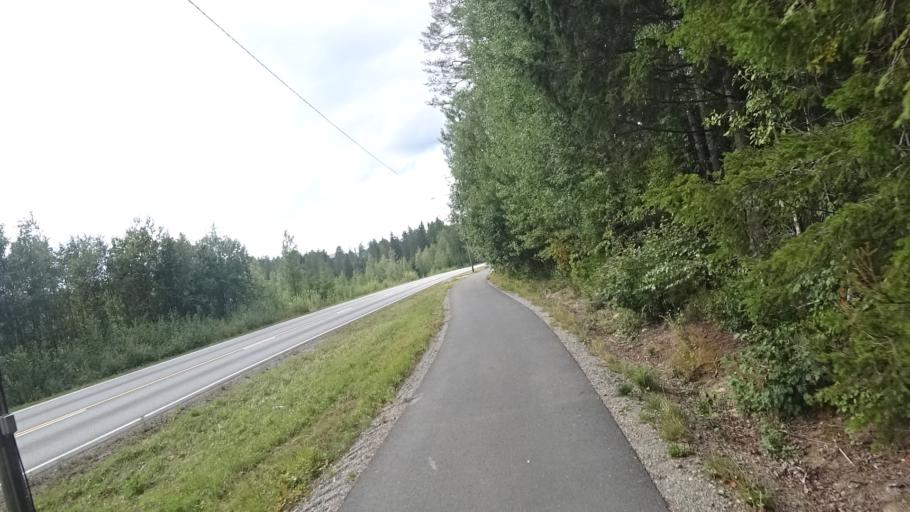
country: FI
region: North Karelia
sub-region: Joensuu
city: Ilomantsi
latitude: 62.6537
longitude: 30.9567
